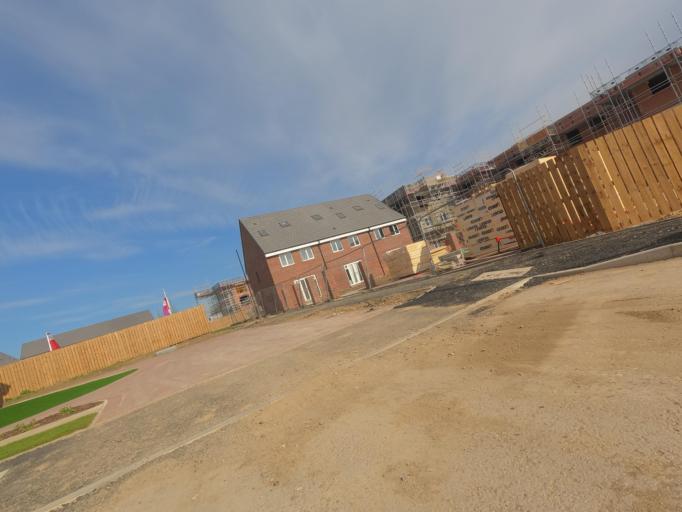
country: GB
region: England
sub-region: Newcastle upon Tyne
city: Dinnington
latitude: 55.0328
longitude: -1.6642
